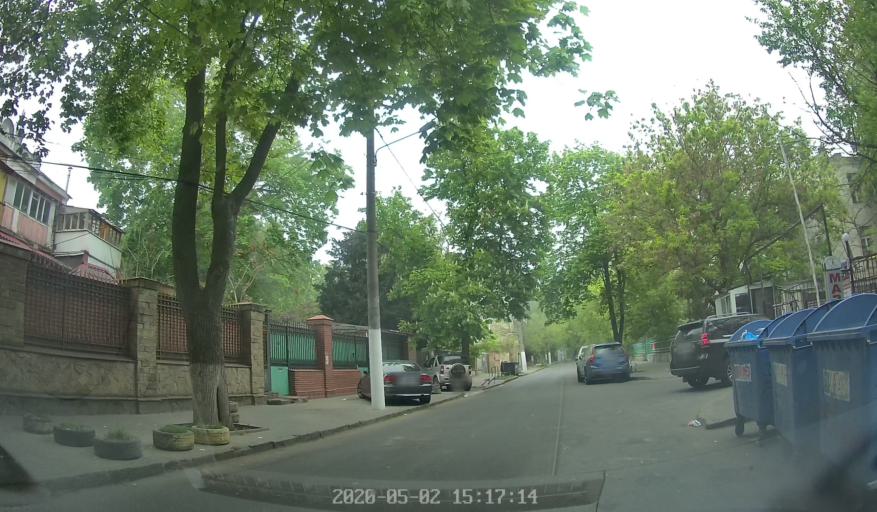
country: NG
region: Niger
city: Lemu
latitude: 9.2947
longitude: 6.1516
